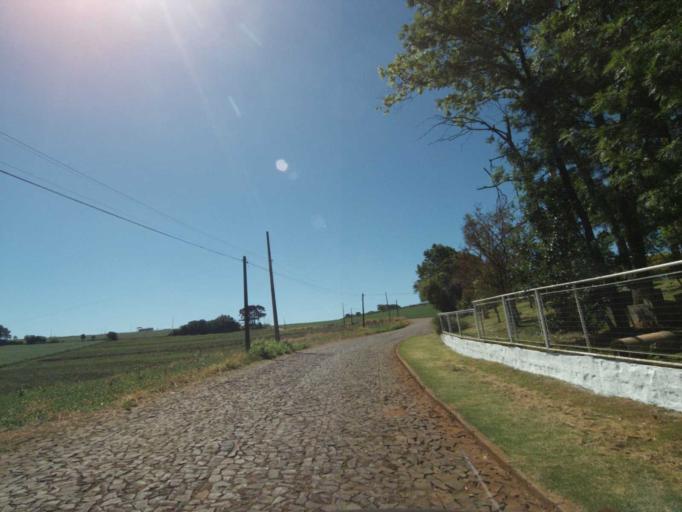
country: BR
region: Parana
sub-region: Coronel Vivida
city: Coronel Vivida
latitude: -25.9604
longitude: -52.8203
